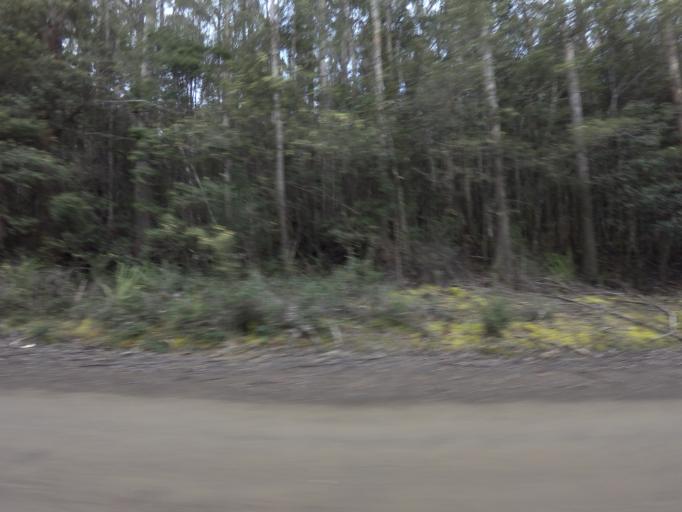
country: AU
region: Tasmania
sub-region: Huon Valley
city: Geeveston
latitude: -43.5259
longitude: 146.8833
